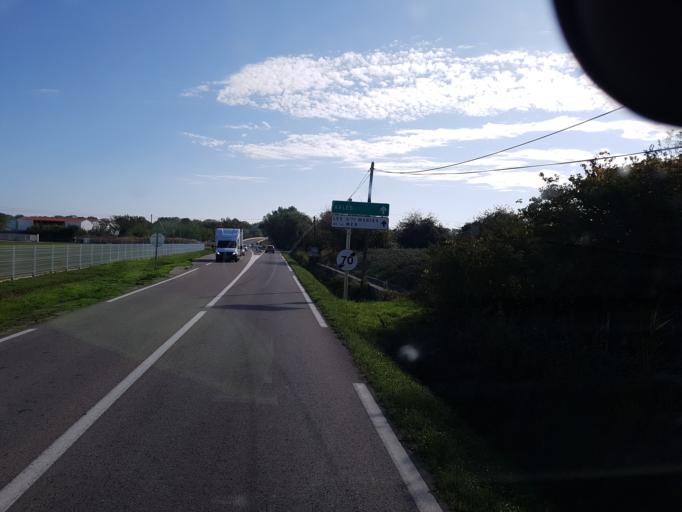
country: FR
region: Languedoc-Roussillon
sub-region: Departement du Gard
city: Saint-Gilles
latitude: 43.6687
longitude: 4.4471
